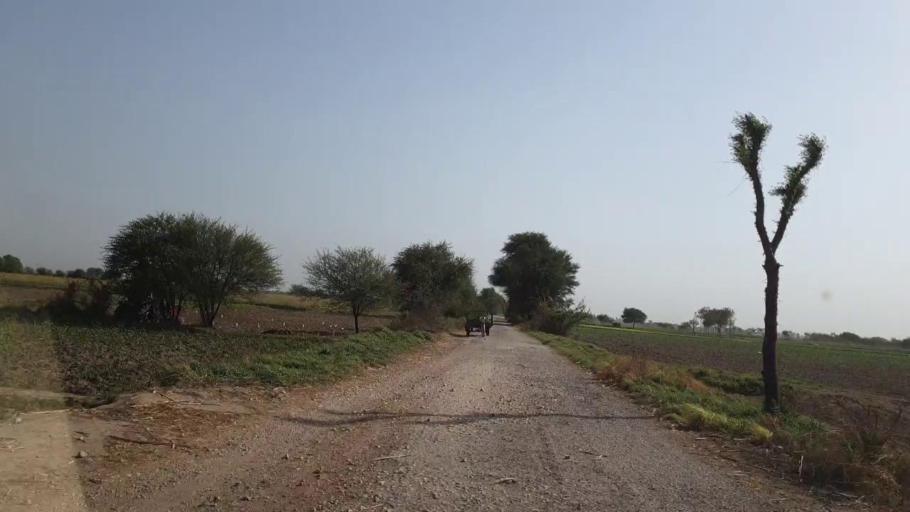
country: PK
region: Sindh
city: Tando Ghulam Ali
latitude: 25.0780
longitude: 68.8369
